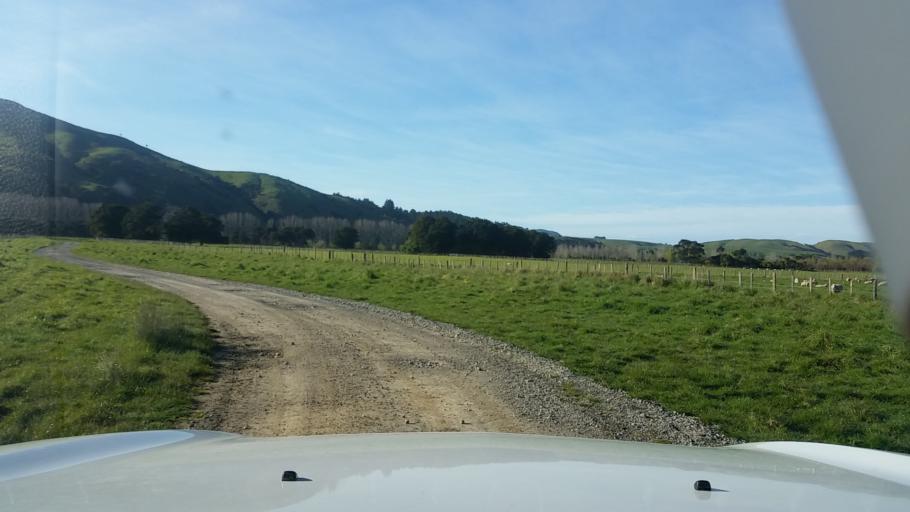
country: NZ
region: Wellington
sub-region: Masterton District
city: Masterton
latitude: -41.1509
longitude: 175.4822
